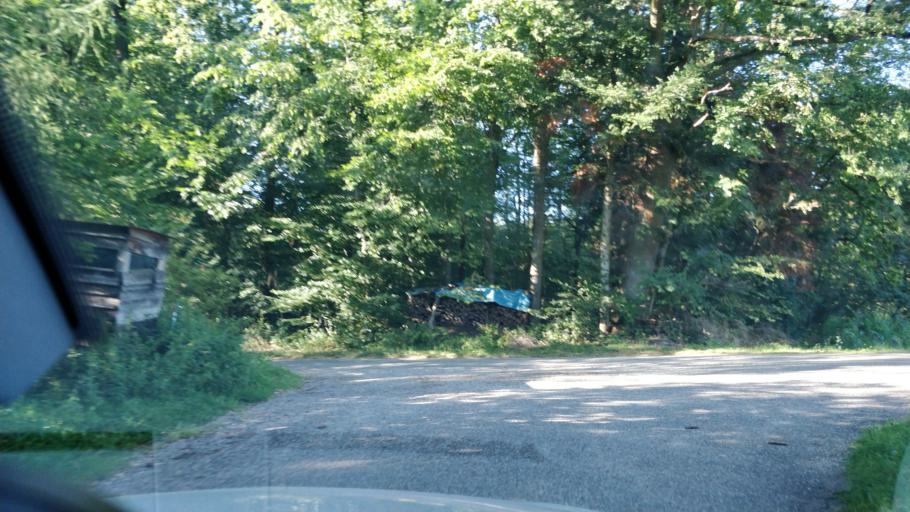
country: DE
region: Baden-Wuerttemberg
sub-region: Regierungsbezirk Stuttgart
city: Murrhardt
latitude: 49.0176
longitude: 9.5839
